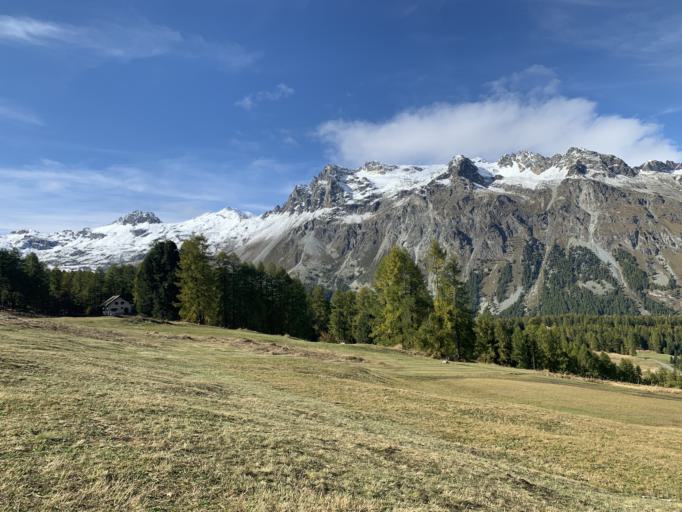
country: CH
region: Grisons
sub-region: Maloja District
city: Silvaplana
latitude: 46.4127
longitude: 9.7615
